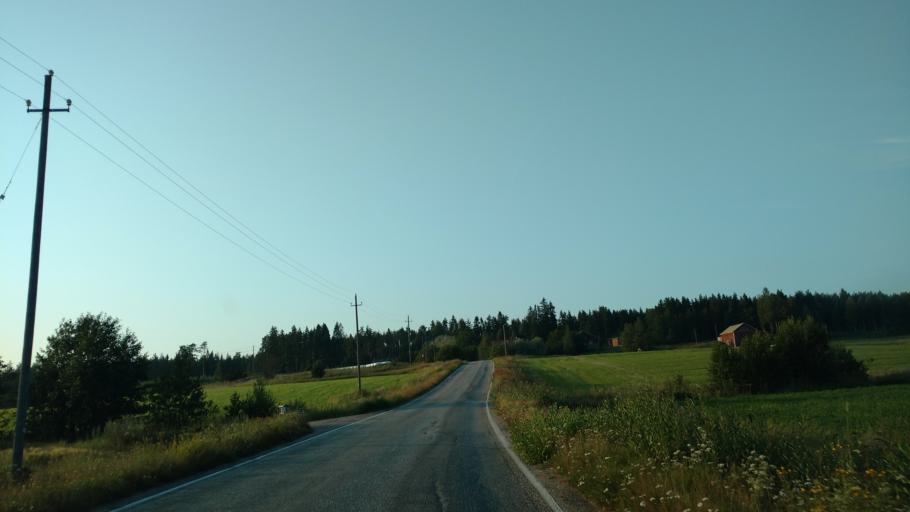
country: FI
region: Varsinais-Suomi
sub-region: Salo
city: Saerkisalo
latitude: 60.1768
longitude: 22.9658
